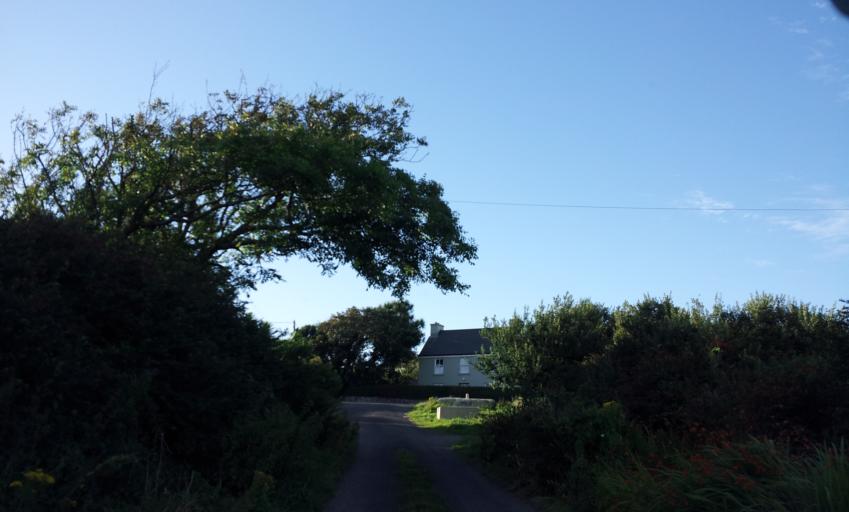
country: IE
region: Munster
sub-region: Ciarrai
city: Dingle
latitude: 52.1231
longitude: -10.3266
